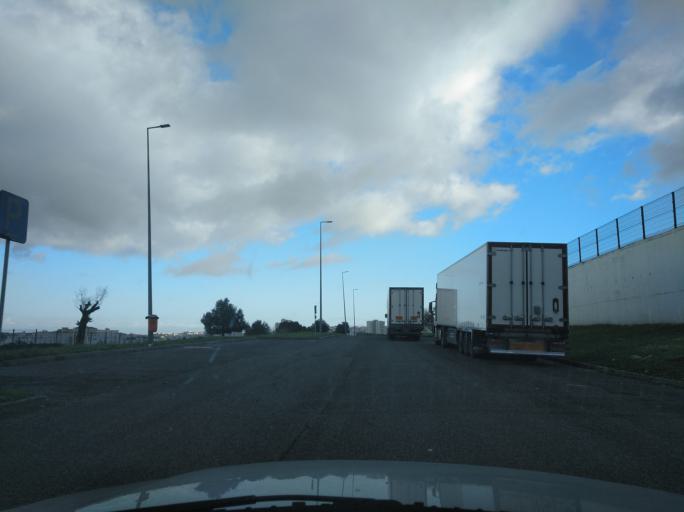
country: PT
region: Lisbon
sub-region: Loures
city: Loures
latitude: 38.8196
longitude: -9.1746
